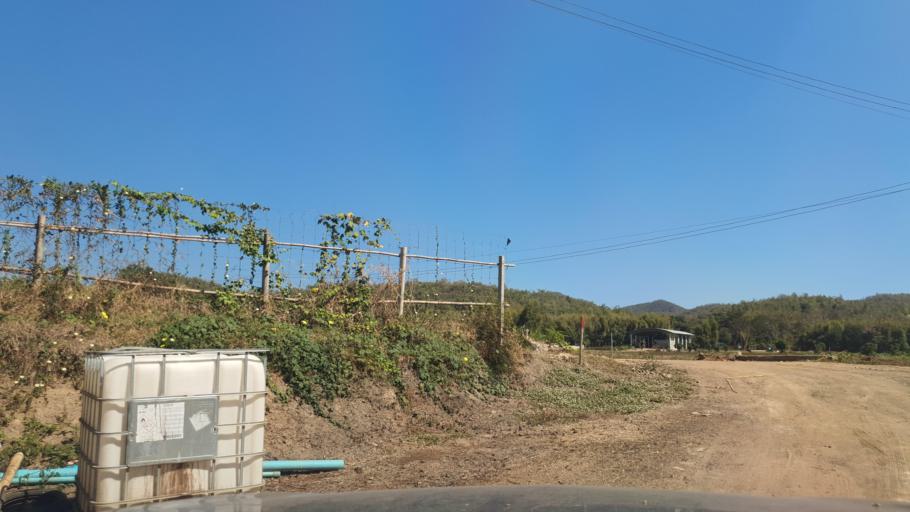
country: TH
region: Chiang Mai
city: Mae Wang
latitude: 18.6831
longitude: 98.8105
